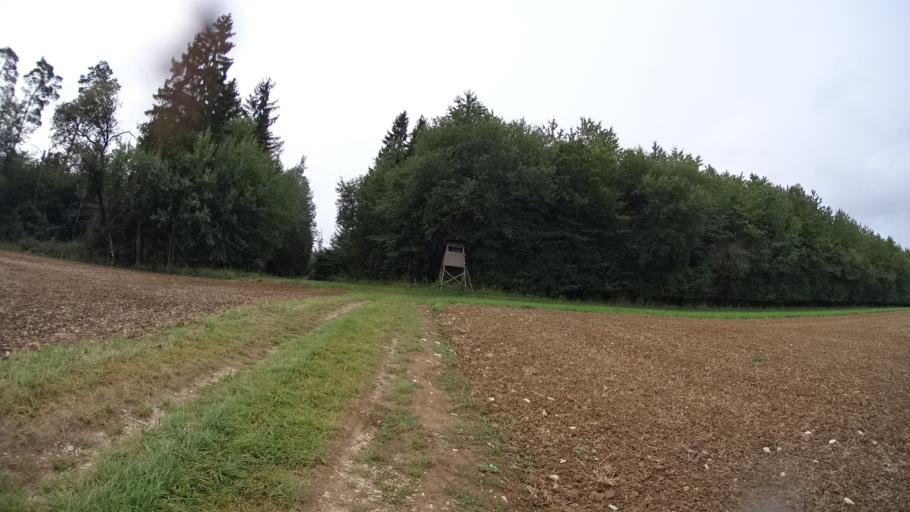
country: DE
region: Bavaria
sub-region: Upper Bavaria
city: Bohmfeld
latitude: 48.8493
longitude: 11.3564
